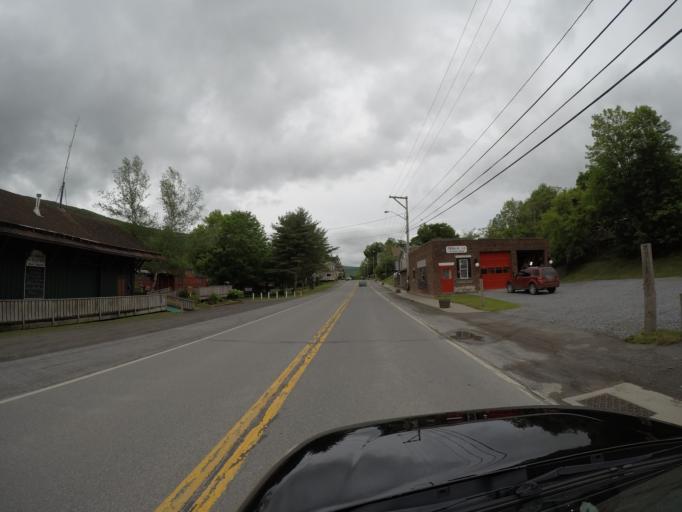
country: US
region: New York
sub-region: Delaware County
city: Stamford
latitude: 42.1476
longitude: -74.6158
